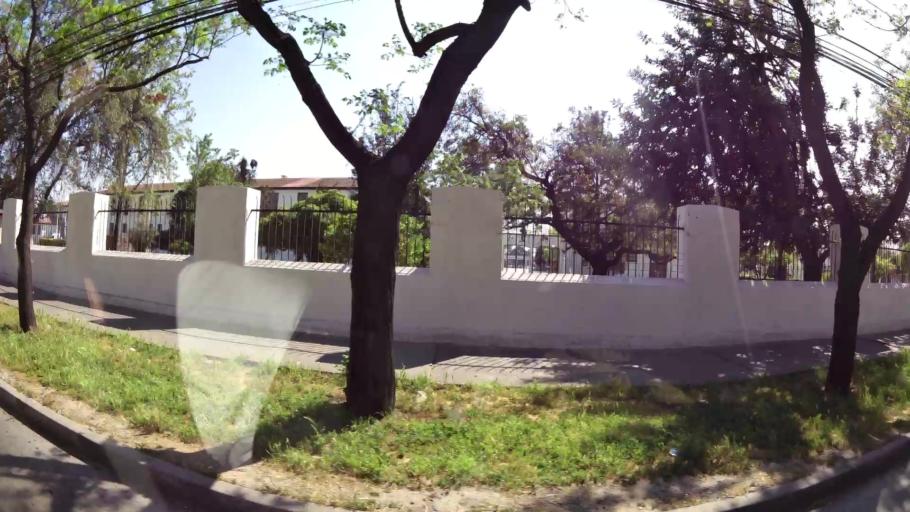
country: CL
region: Santiago Metropolitan
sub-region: Provincia de Maipo
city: San Bernardo
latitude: -33.5857
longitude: -70.7006
